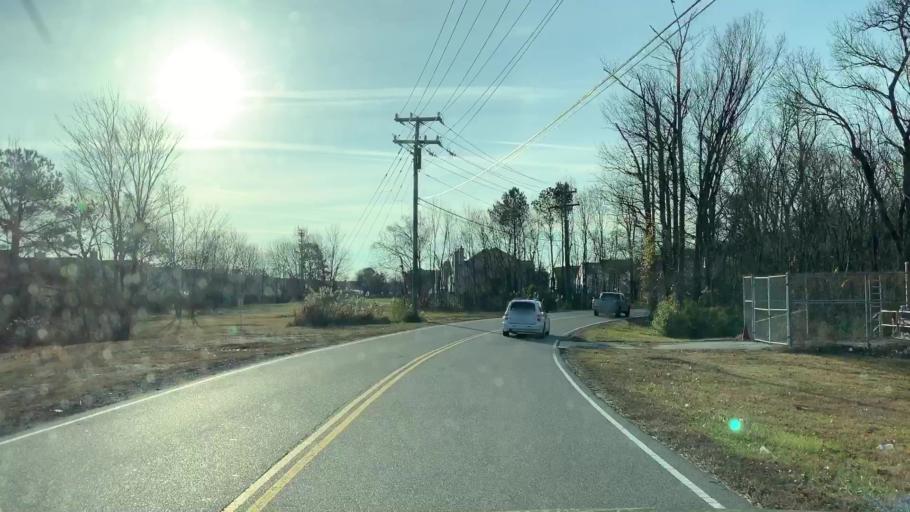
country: US
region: Virginia
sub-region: City of Chesapeake
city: Chesapeake
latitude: 36.7834
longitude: -76.1589
